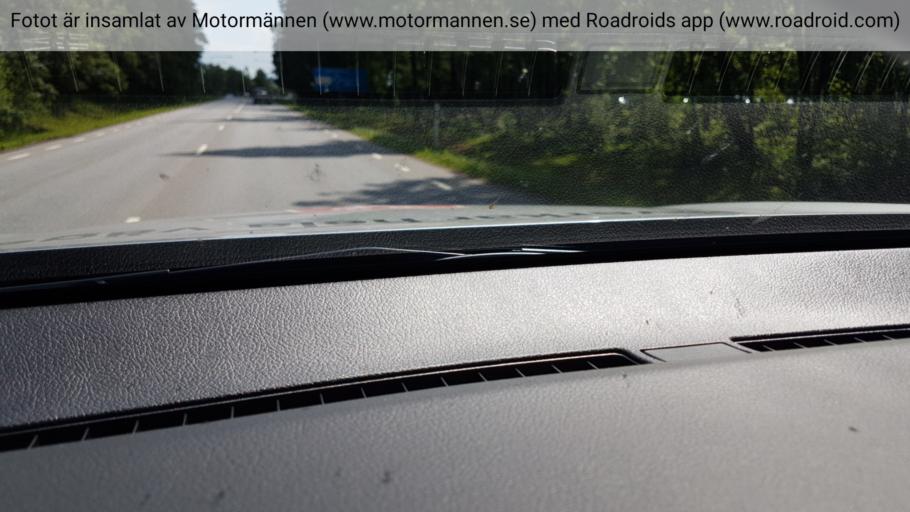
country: SE
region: Vaestra Goetaland
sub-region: Lidkopings Kommun
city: Lidkoping
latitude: 58.4950
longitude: 13.1366
